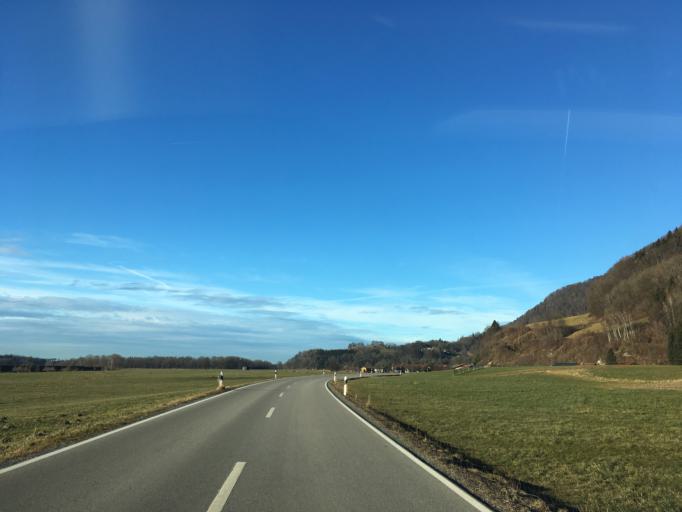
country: AT
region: Tyrol
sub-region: Politischer Bezirk Kufstein
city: Erl
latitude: 47.7062
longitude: 12.1641
